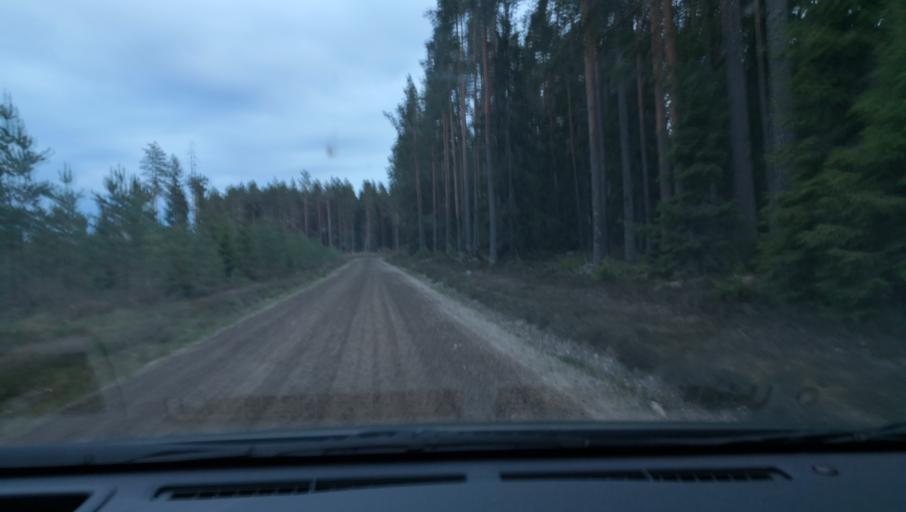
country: SE
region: Vaestmanland
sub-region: Skinnskattebergs Kommun
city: Skinnskatteberg
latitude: 59.7137
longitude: 15.5123
